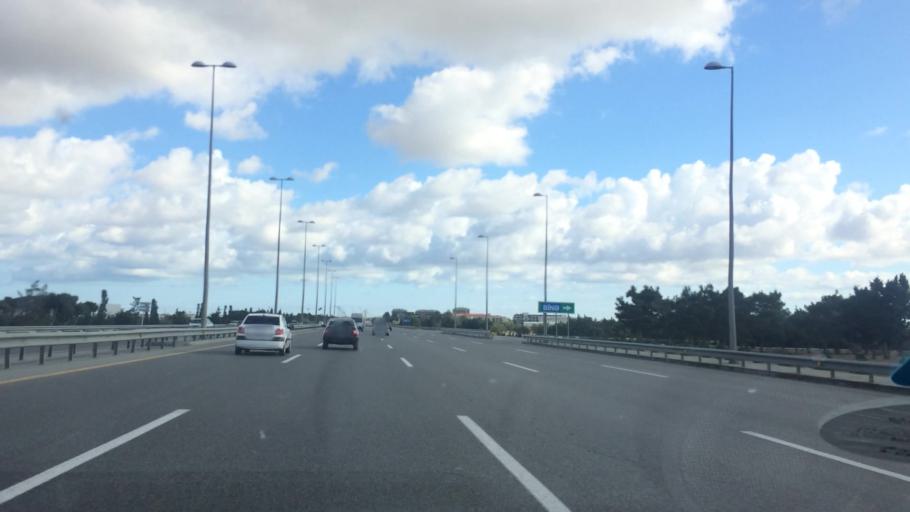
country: AZ
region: Baki
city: Biny Selo
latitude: 40.4498
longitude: 50.0588
